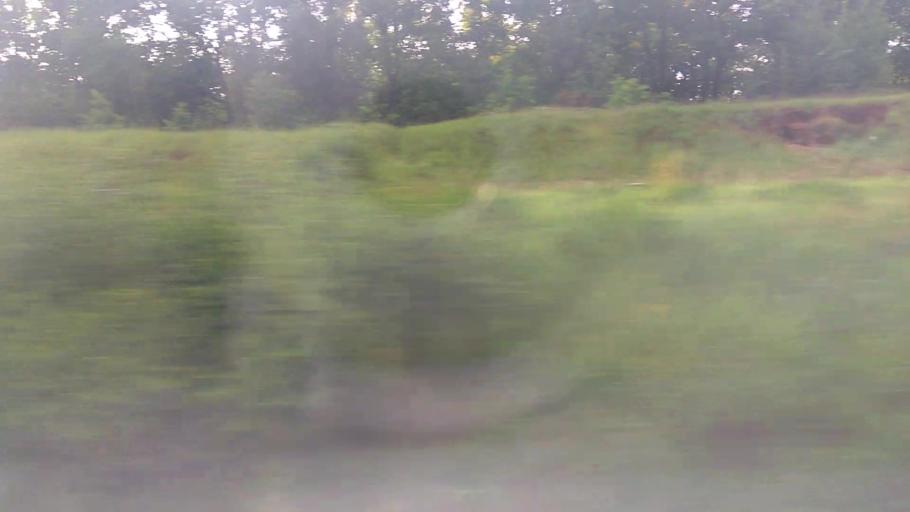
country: RU
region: Moskovskaya
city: Kashira
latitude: 54.8691
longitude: 38.1393
